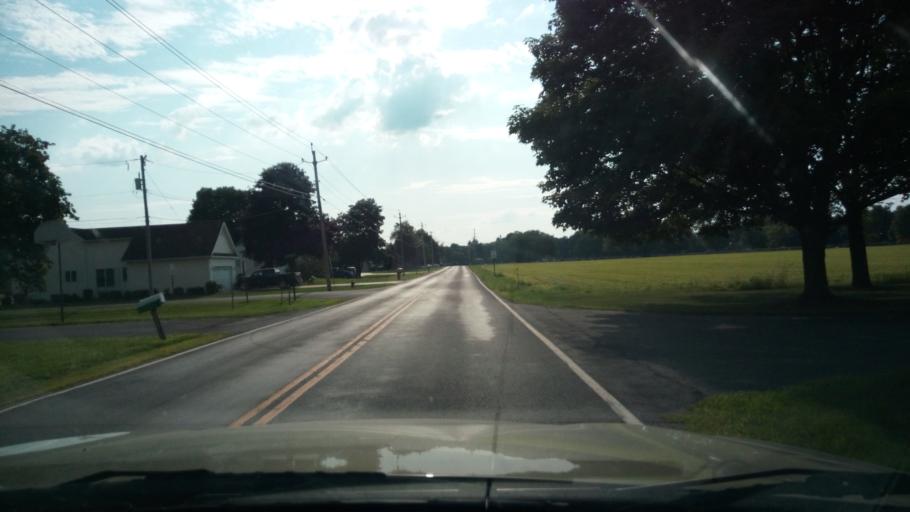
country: US
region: New York
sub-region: Wayne County
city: Lyons
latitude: 43.0463
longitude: -76.9881
